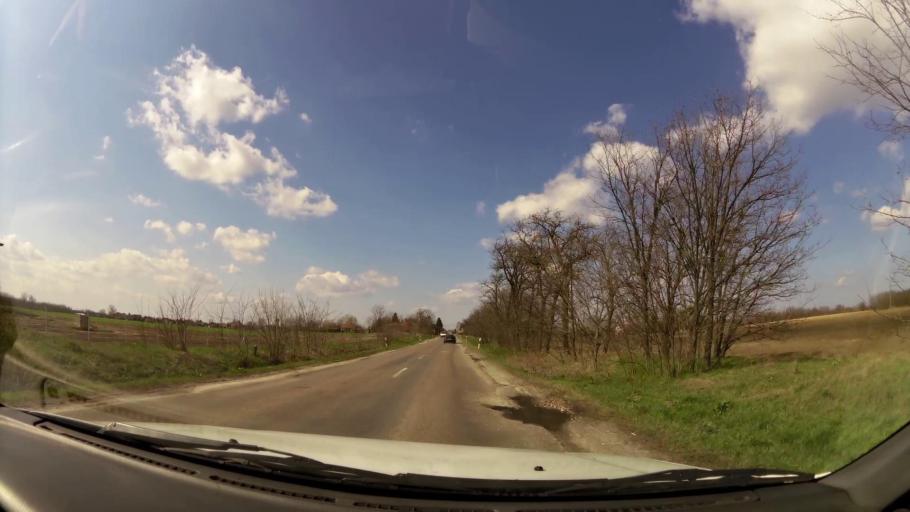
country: HU
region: Pest
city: Farmos
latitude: 47.3522
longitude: 19.8573
